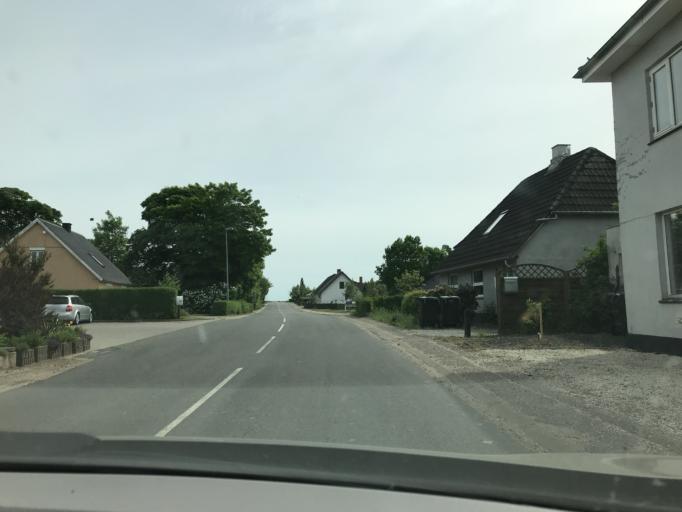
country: DK
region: Central Jutland
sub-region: Norddjurs Kommune
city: Allingabro
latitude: 56.5500
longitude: 10.2995
